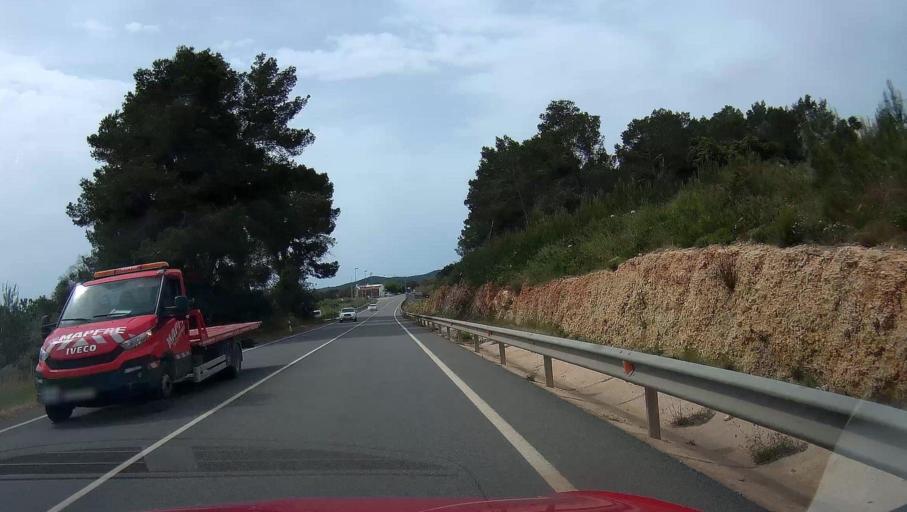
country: ES
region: Balearic Islands
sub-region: Illes Balears
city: Sant Joan de Labritja
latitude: 39.0358
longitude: 1.4911
